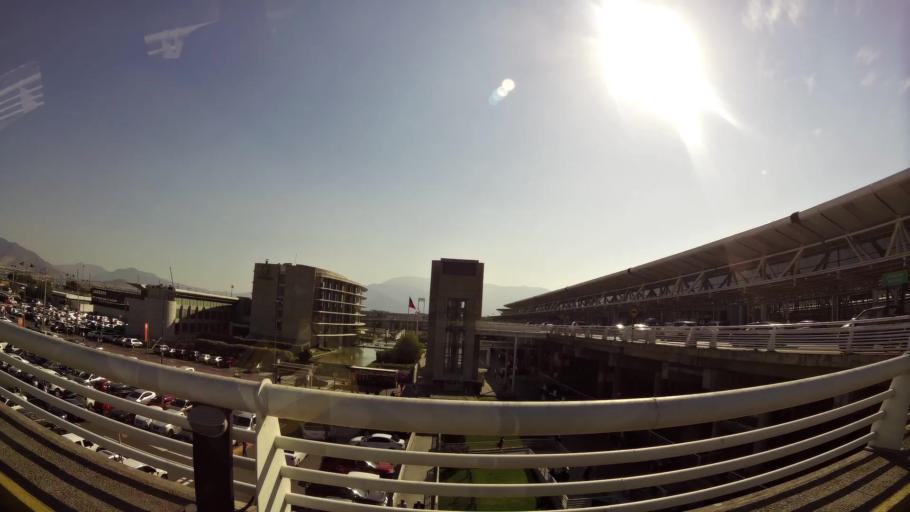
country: CL
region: Santiago Metropolitan
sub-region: Provincia de Santiago
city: Lo Prado
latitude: -33.3974
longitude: -70.7924
